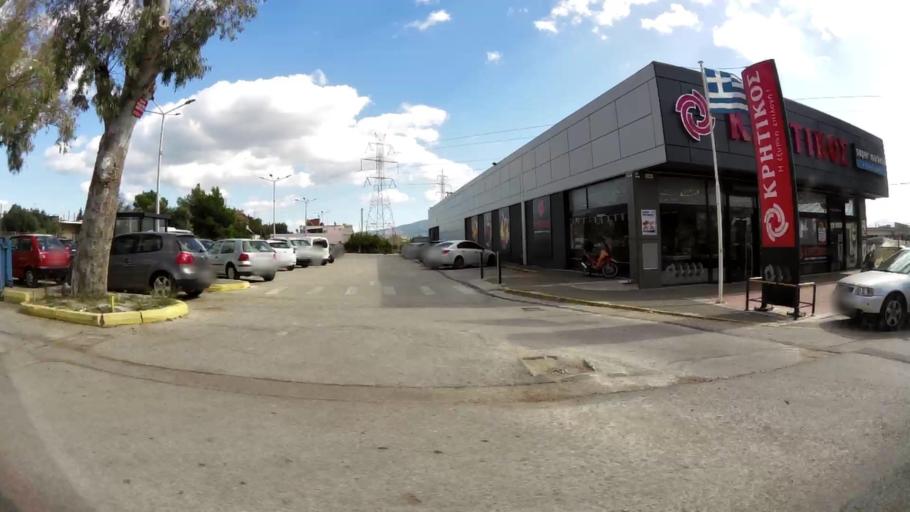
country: GR
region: Attica
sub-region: Nomarchia Anatolikis Attikis
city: Acharnes
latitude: 38.1069
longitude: 23.7431
